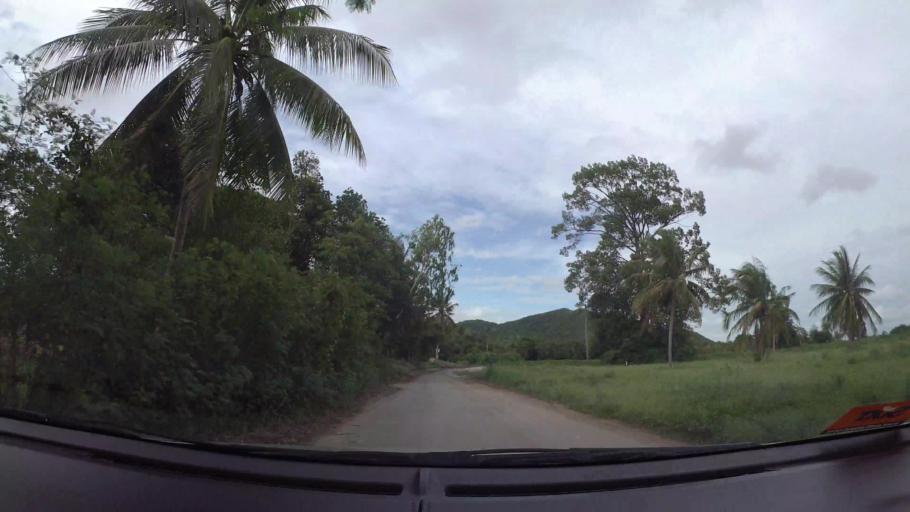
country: TH
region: Chon Buri
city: Sattahip
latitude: 12.7167
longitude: 100.9104
